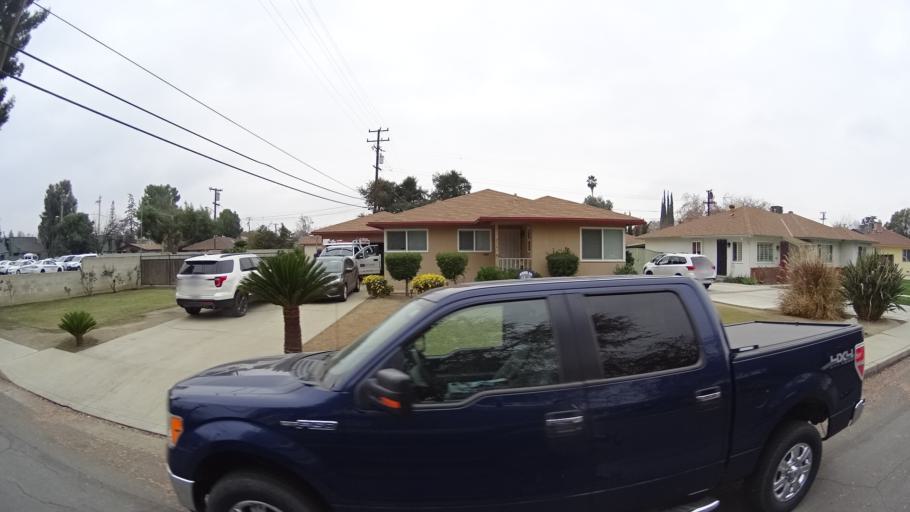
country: US
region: California
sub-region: Kern County
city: Bakersfield
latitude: 35.3822
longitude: -119.0258
